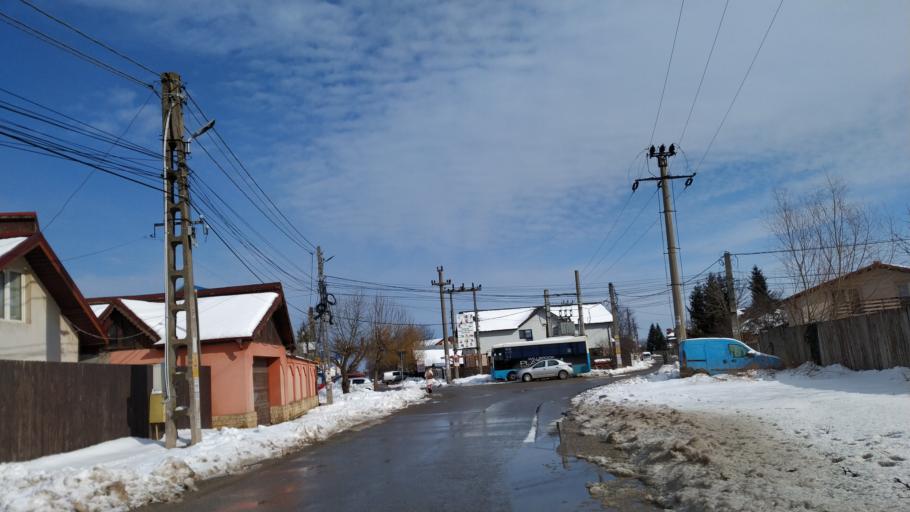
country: RO
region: Ilfov
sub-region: Comuna Berceni
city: Berceni
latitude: 44.3179
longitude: 26.1899
